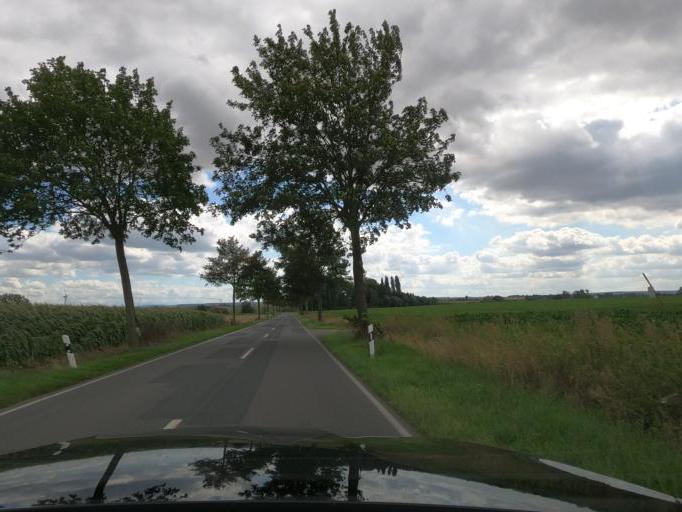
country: DE
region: Lower Saxony
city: Ilsede
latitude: 52.2357
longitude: 10.1711
